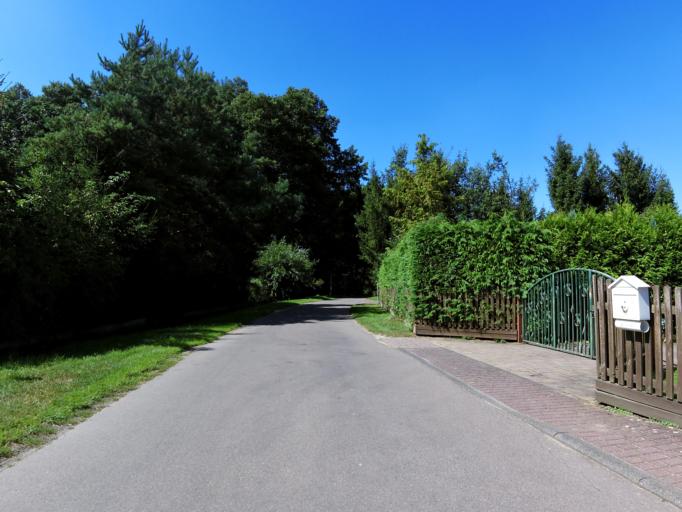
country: DE
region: Saxony
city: Torgau
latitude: 51.5125
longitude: 13.0268
